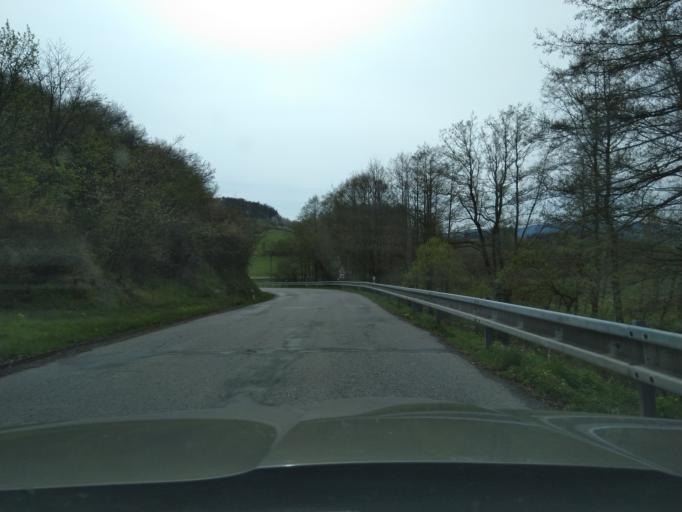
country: CZ
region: Plzensky
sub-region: Okres Klatovy
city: Susice
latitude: 49.2213
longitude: 13.6125
